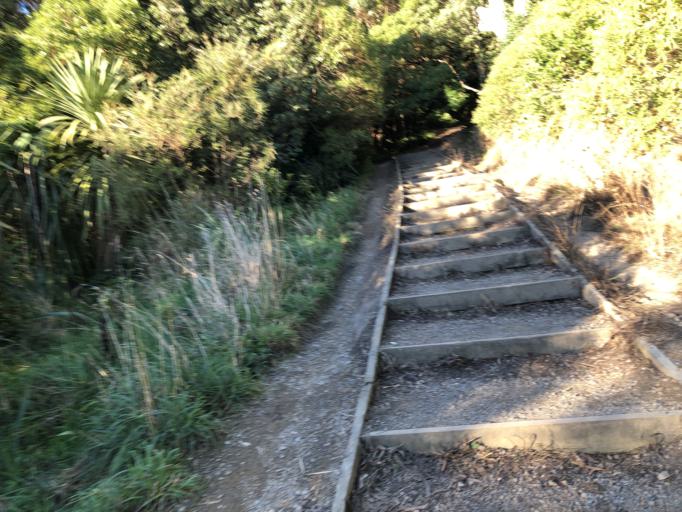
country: NZ
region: Wellington
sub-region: Wellington City
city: Wellington
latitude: -41.2988
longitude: 174.7893
